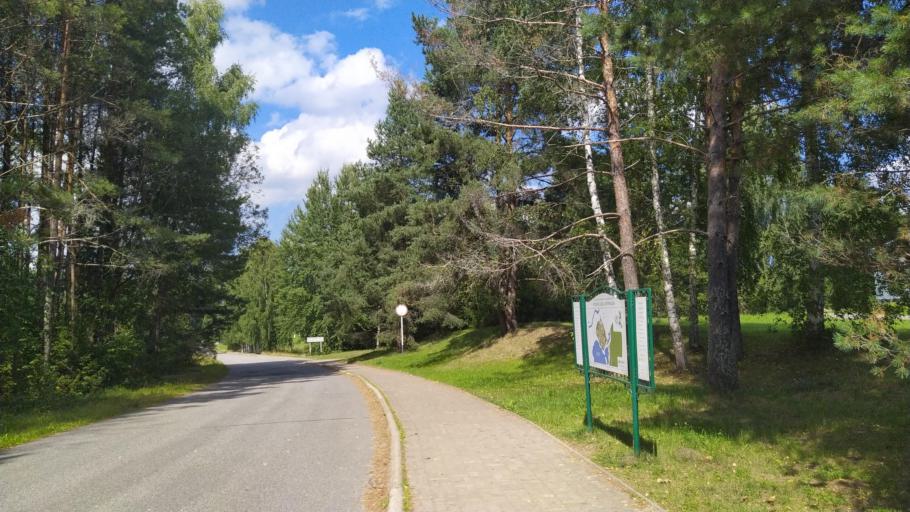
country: RU
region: Pskov
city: Pushkinskiye Gory
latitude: 57.0758
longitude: 28.9560
